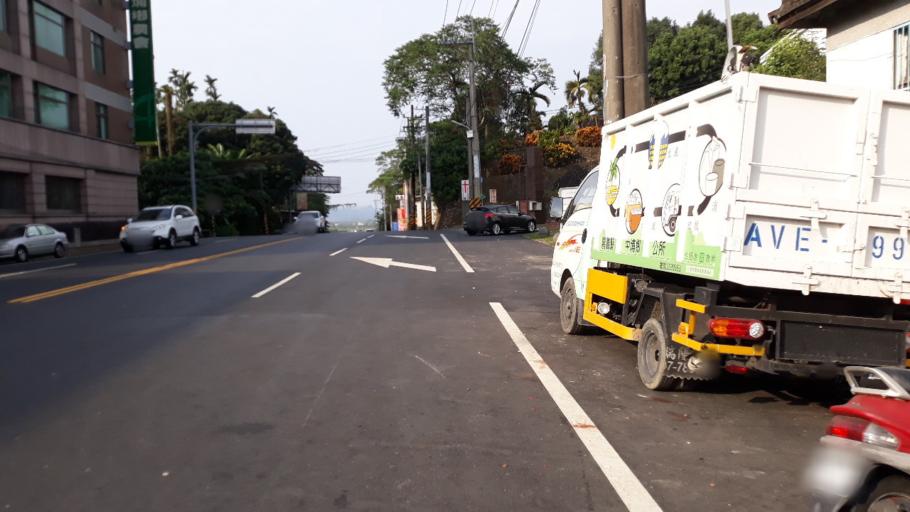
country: TW
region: Taiwan
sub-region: Chiayi
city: Jiayi Shi
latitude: 23.4253
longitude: 120.5235
